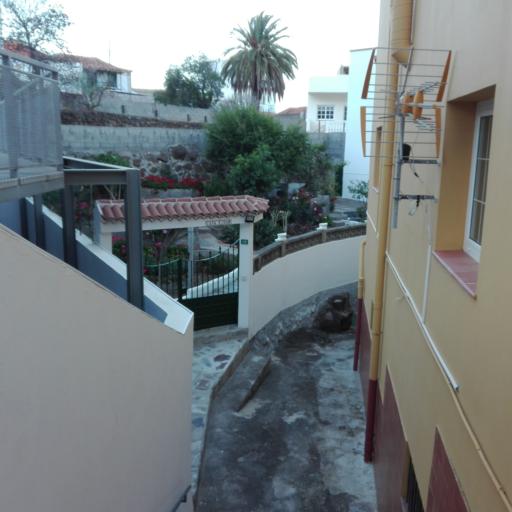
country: ES
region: Canary Islands
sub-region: Provincia de Santa Cruz de Tenerife
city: Candelaria
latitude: 28.4019
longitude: -16.3608
